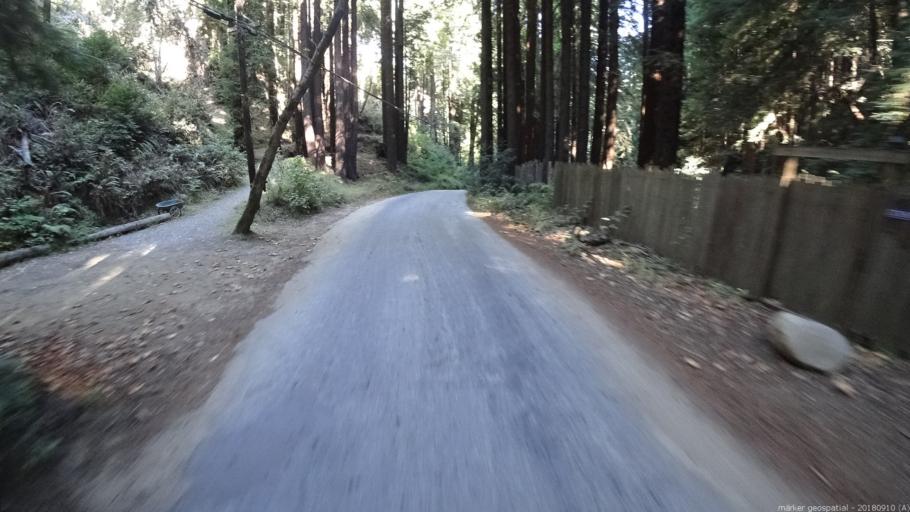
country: US
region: California
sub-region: Monterey County
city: Carmel Valley Village
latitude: 36.3925
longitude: -121.8769
